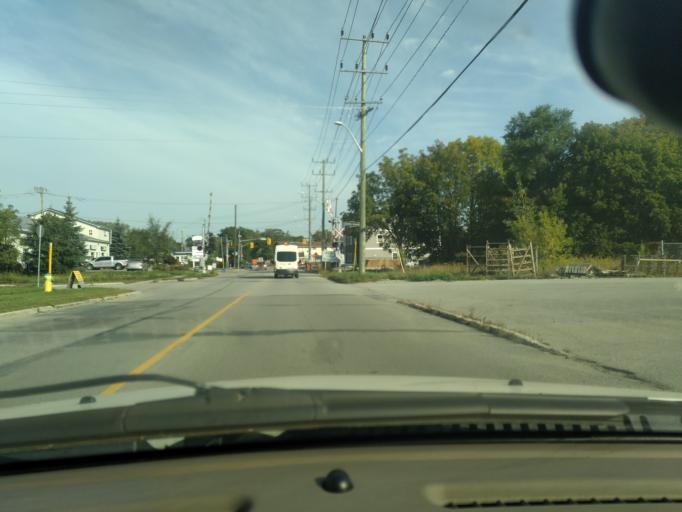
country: CA
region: Ontario
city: Barrie
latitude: 44.3727
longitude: -79.6937
